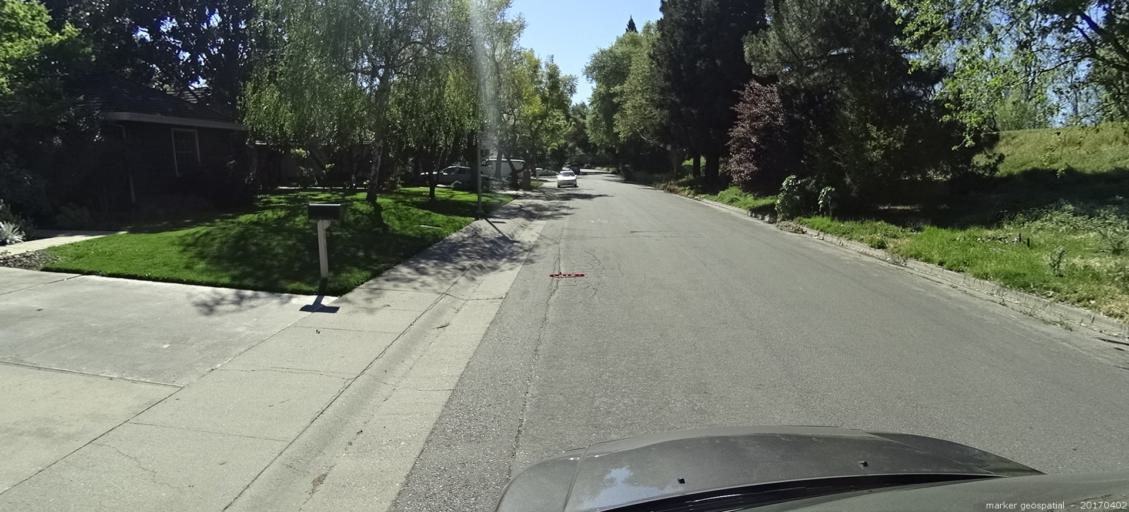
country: US
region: California
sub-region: Yolo County
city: West Sacramento
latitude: 38.5138
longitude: -121.5461
